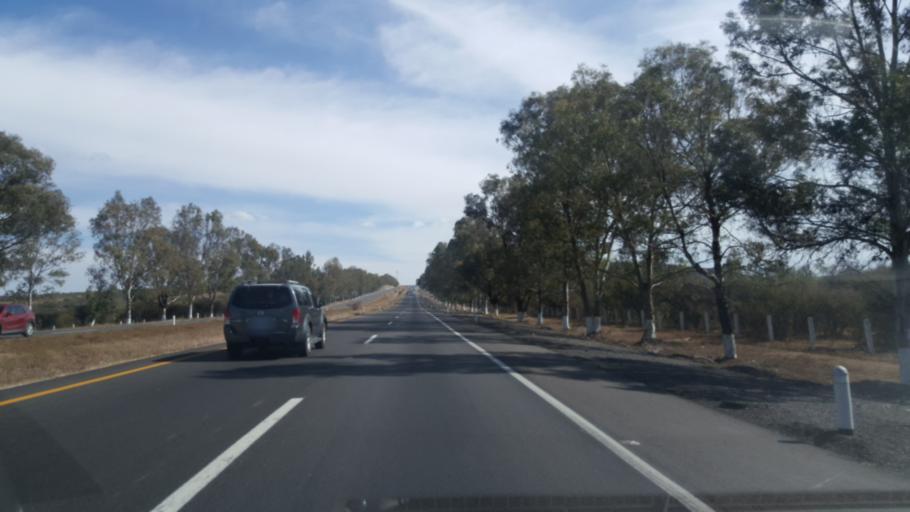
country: MX
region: Jalisco
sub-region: Lagos de Moreno
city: Cristeros [Fraccionamiento]
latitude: 21.2705
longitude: -101.9735
